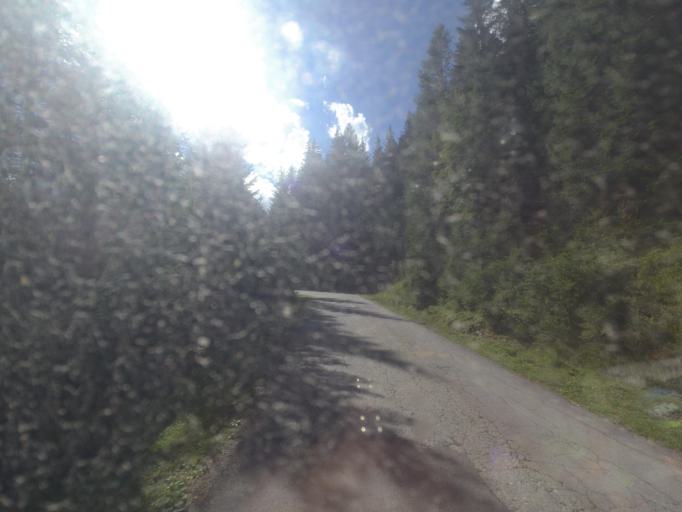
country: AT
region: Salzburg
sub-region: Politischer Bezirk Tamsweg
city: Zederhaus
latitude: 47.1850
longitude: 13.3987
